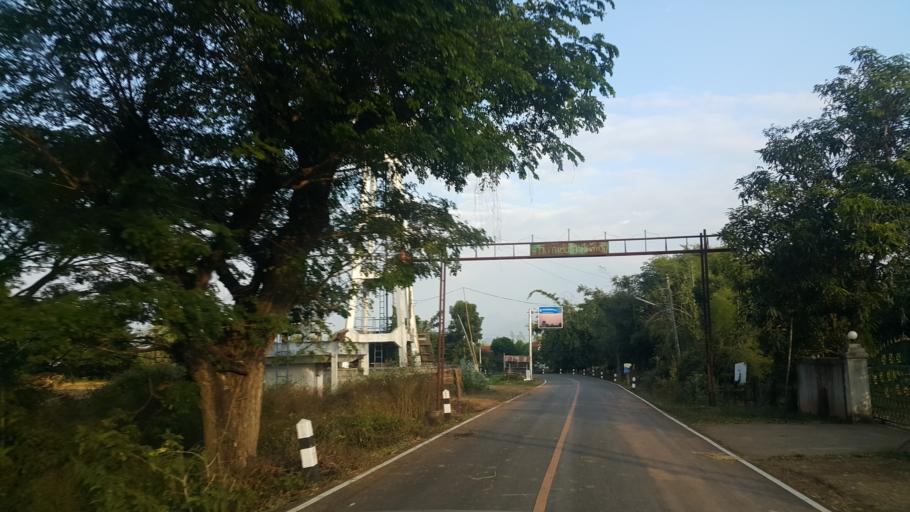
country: TH
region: Lampang
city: Sop Prap
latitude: 17.9430
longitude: 99.3393
